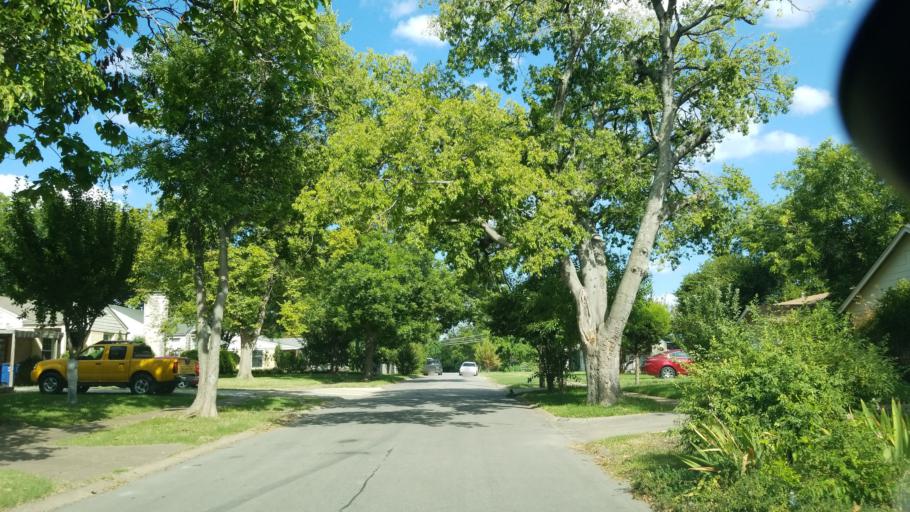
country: US
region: Texas
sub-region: Dallas County
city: Dallas
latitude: 32.7730
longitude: -96.7124
